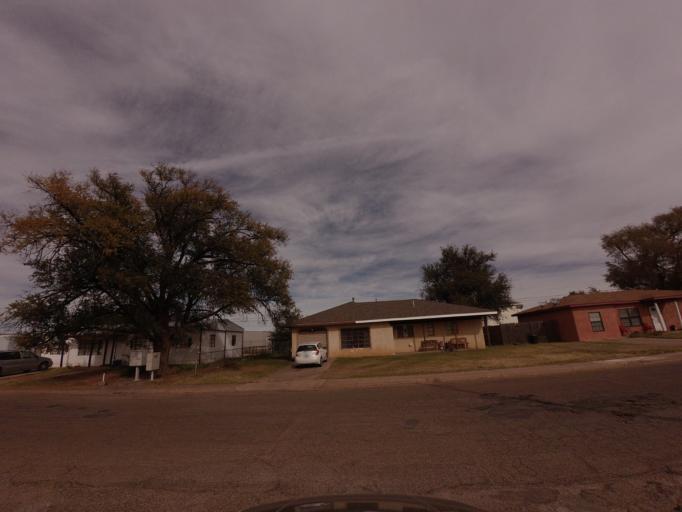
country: US
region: New Mexico
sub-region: Curry County
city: Clovis
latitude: 34.4300
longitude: -103.2104
